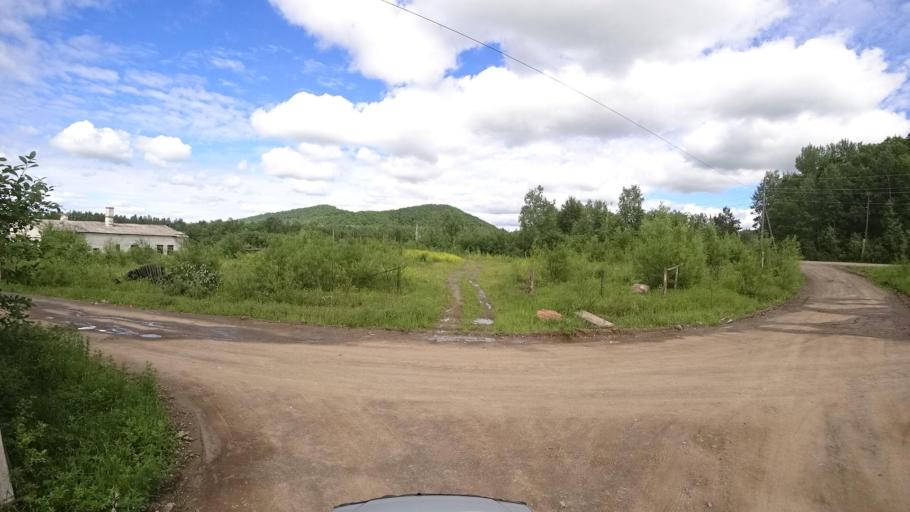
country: RU
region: Khabarovsk Krai
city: Litovko
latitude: 49.3686
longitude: 135.1767
